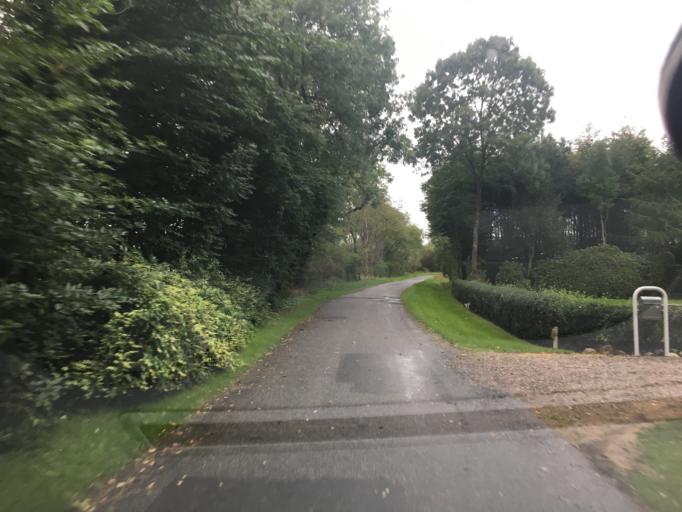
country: DE
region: Schleswig-Holstein
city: Ellhoft
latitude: 54.9379
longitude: 8.9539
